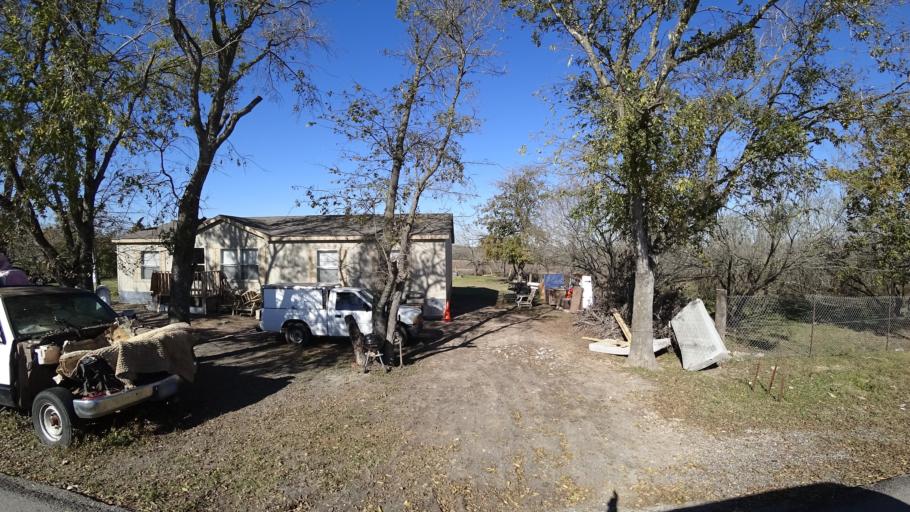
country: US
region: Texas
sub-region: Travis County
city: Garfield
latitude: 30.1139
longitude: -97.6229
